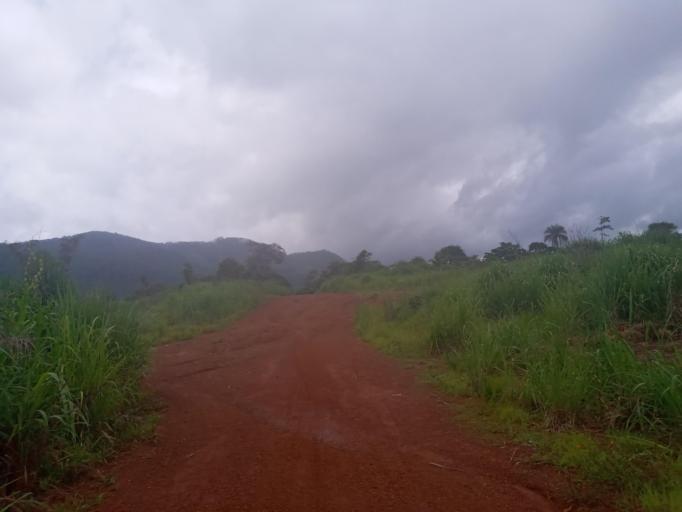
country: SL
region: Northern Province
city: Bumbuna
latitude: 8.9492
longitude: -11.7556
